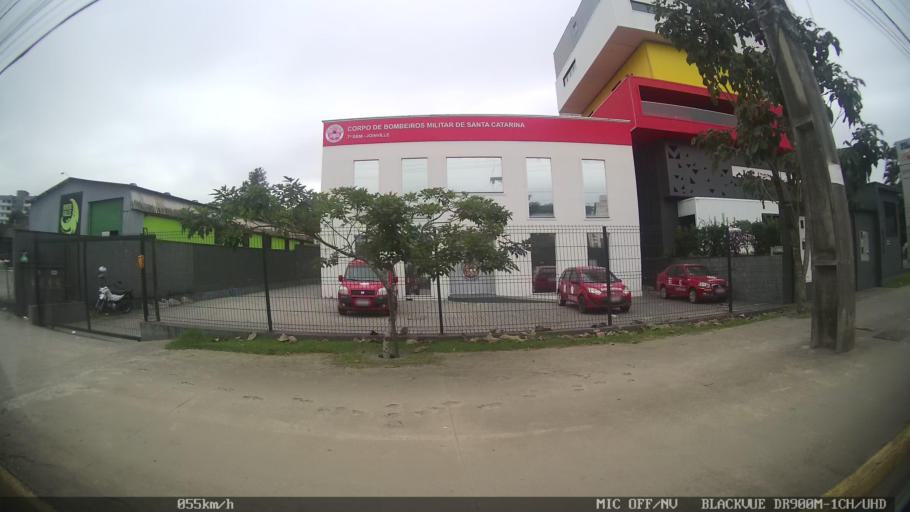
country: BR
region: Santa Catarina
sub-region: Joinville
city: Joinville
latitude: -26.2557
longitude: -48.8515
